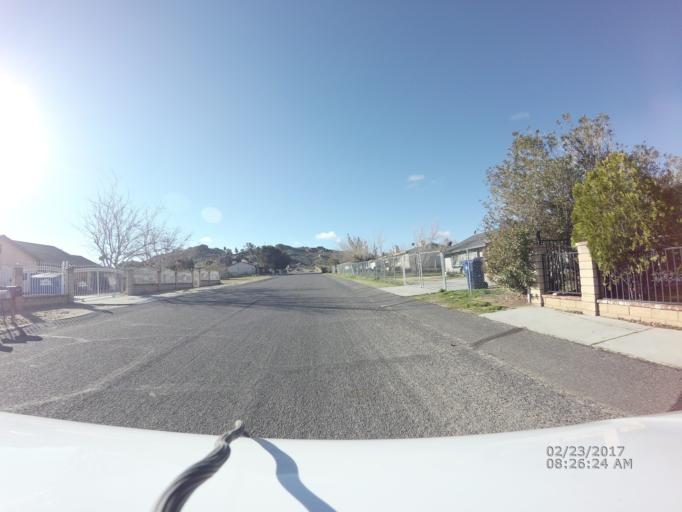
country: US
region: California
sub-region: Los Angeles County
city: Lake Los Angeles
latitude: 34.6116
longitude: -117.8296
